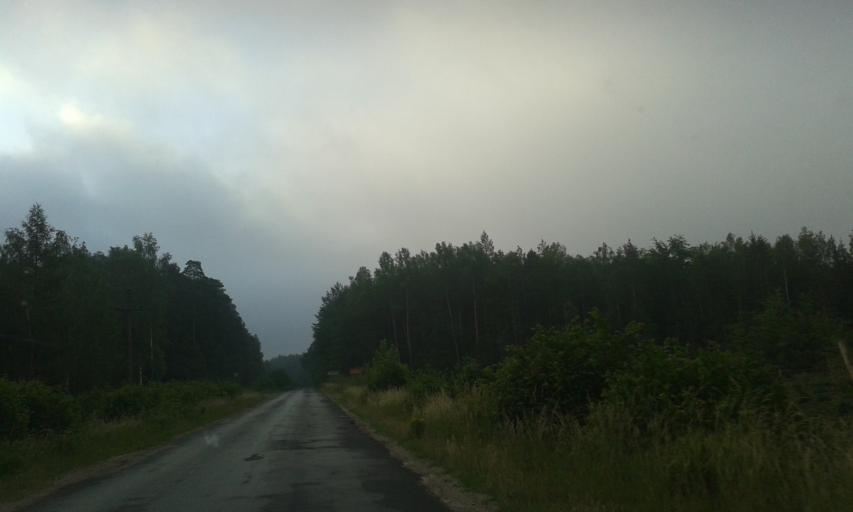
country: PL
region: Kujawsko-Pomorskie
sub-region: Powiat sepolenski
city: Sypniewo
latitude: 53.4539
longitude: 17.3501
